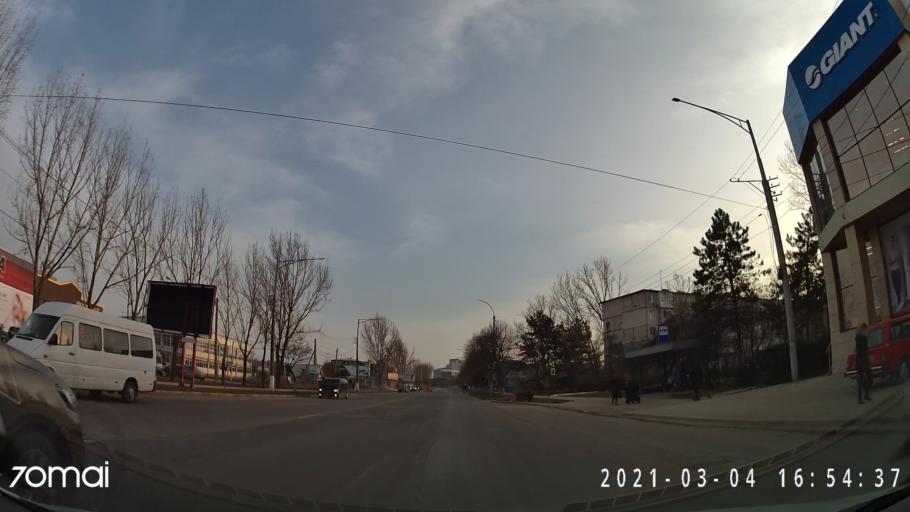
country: MD
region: Balti
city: Balti
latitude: 47.7635
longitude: 27.9412
